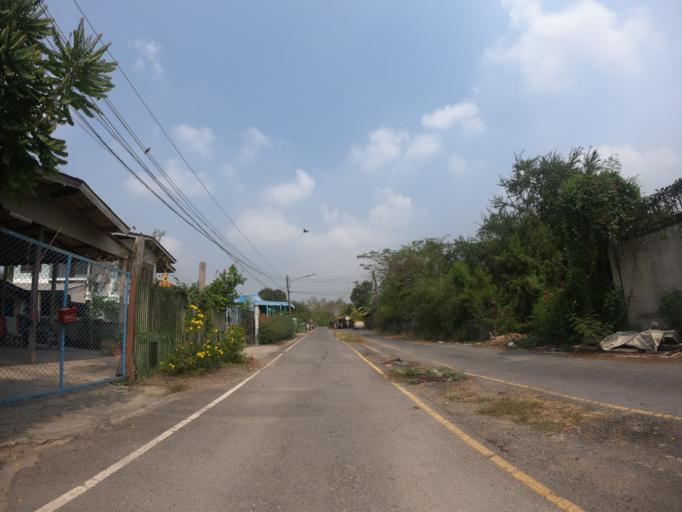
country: TH
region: Pathum Thani
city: Nong Suea
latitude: 14.0652
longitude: 100.8501
